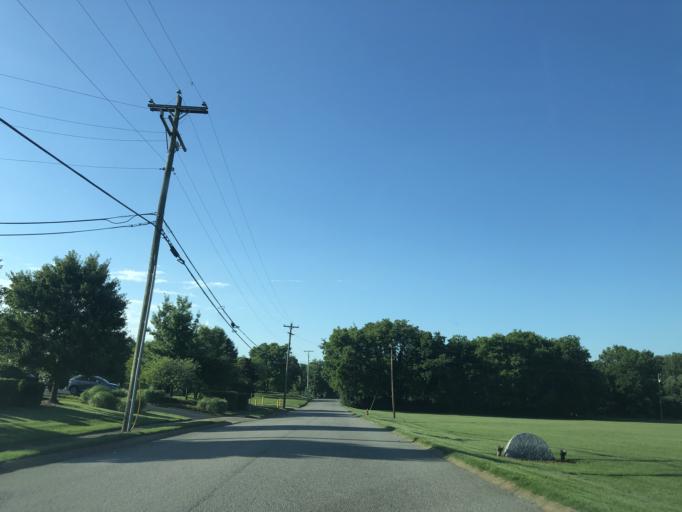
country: US
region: Tennessee
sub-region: Davidson County
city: Nashville
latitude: 36.2066
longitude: -86.8658
